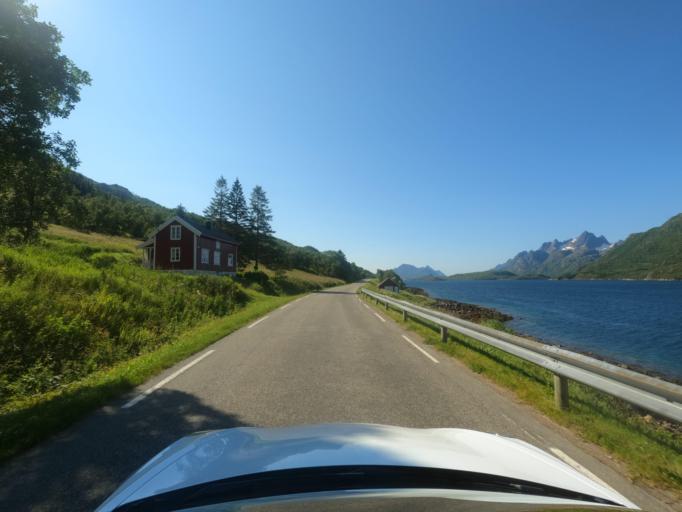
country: NO
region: Nordland
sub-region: Hadsel
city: Stokmarknes
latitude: 68.3819
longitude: 15.0895
